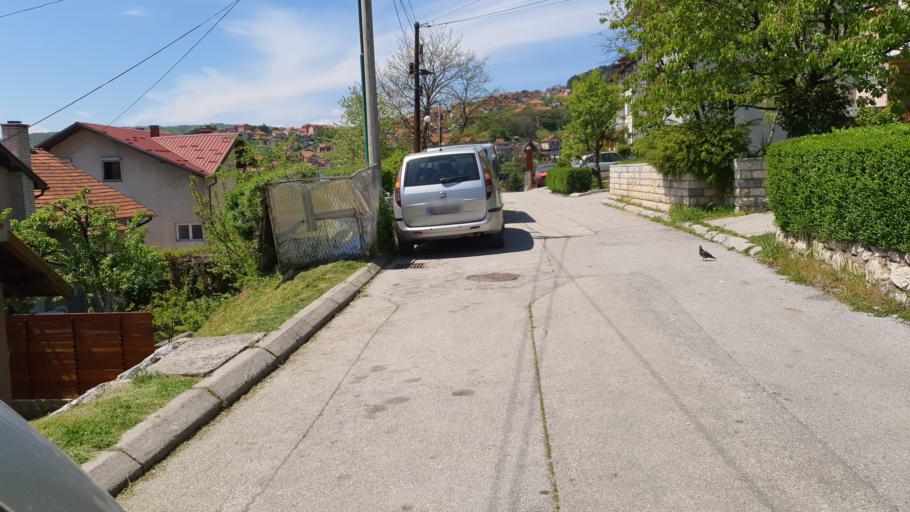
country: RS
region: Central Serbia
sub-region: Zlatiborski Okrug
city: Uzice
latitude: 43.8606
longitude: 19.8438
